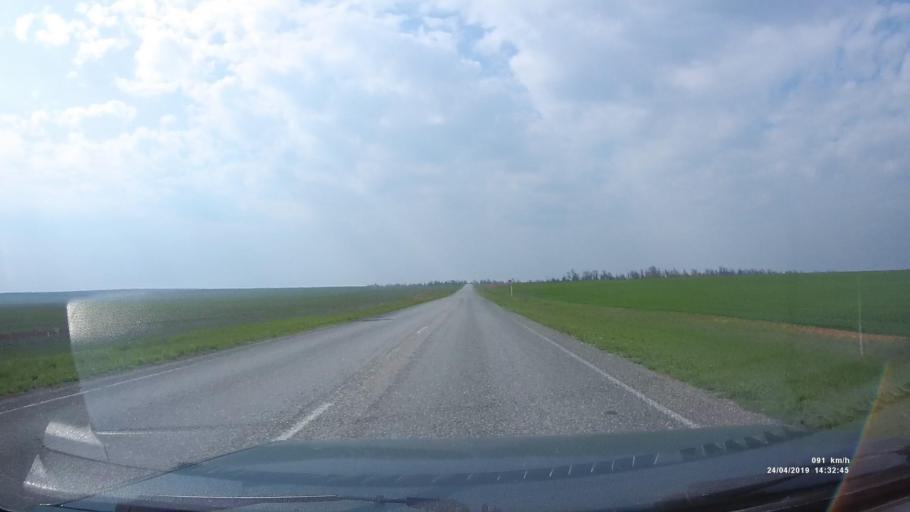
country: RU
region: Kalmykiya
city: Arshan'
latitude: 46.3673
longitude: 43.9643
